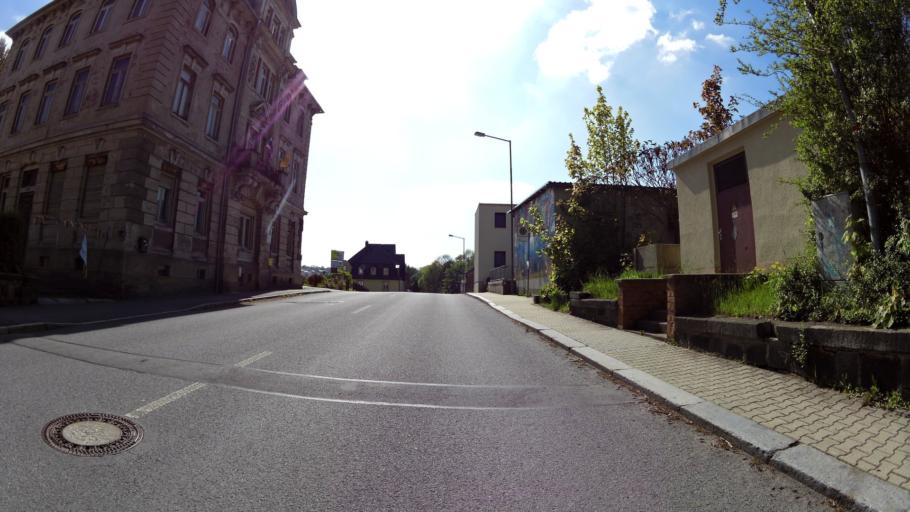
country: DE
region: Saxony
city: Sebnitz
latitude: 50.9760
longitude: 14.2765
